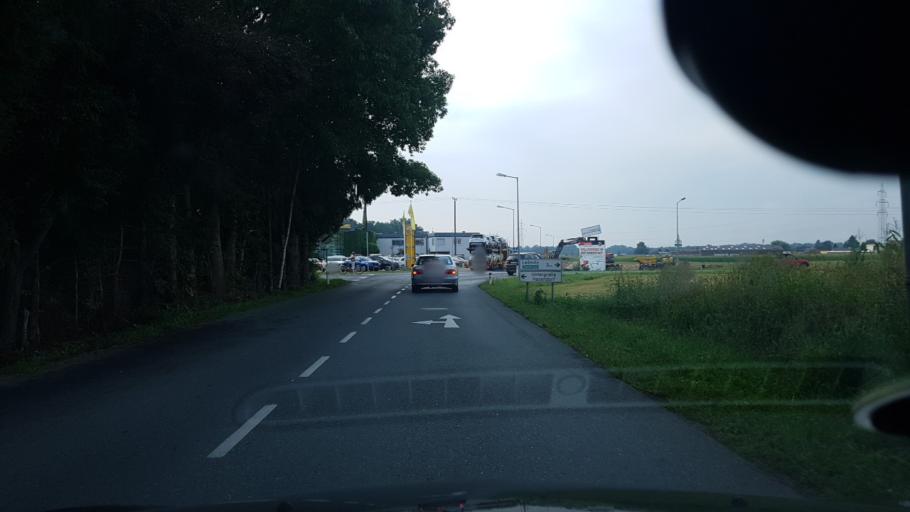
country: AT
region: Styria
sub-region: Politischer Bezirk Leibnitz
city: Kaindorf an der Sulm
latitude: 46.8020
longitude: 15.5634
